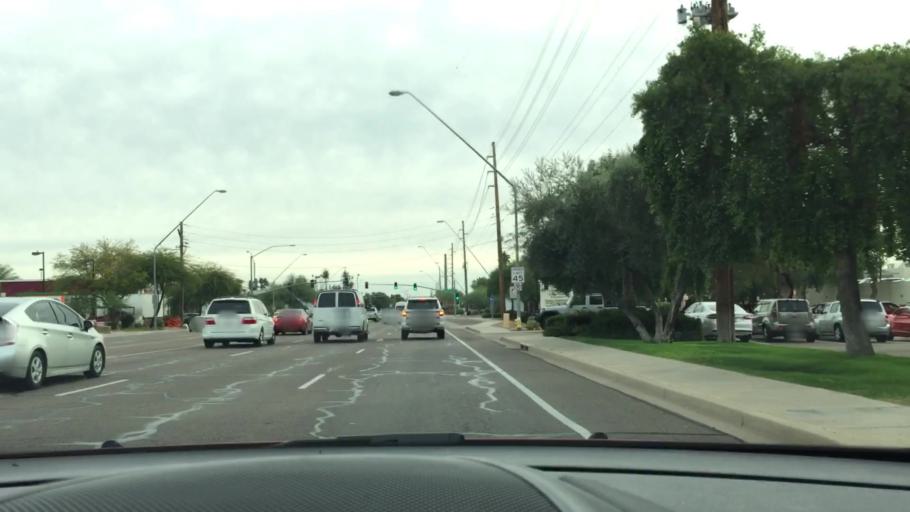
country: US
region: Arizona
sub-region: Maricopa County
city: Gilbert
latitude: 33.4118
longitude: -111.6847
